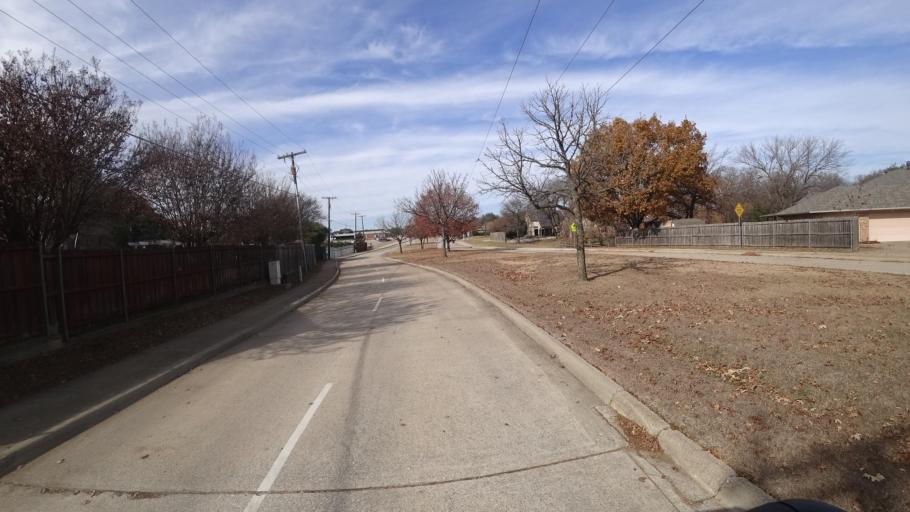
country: US
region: Texas
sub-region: Denton County
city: Highland Village
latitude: 33.0810
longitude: -97.0412
